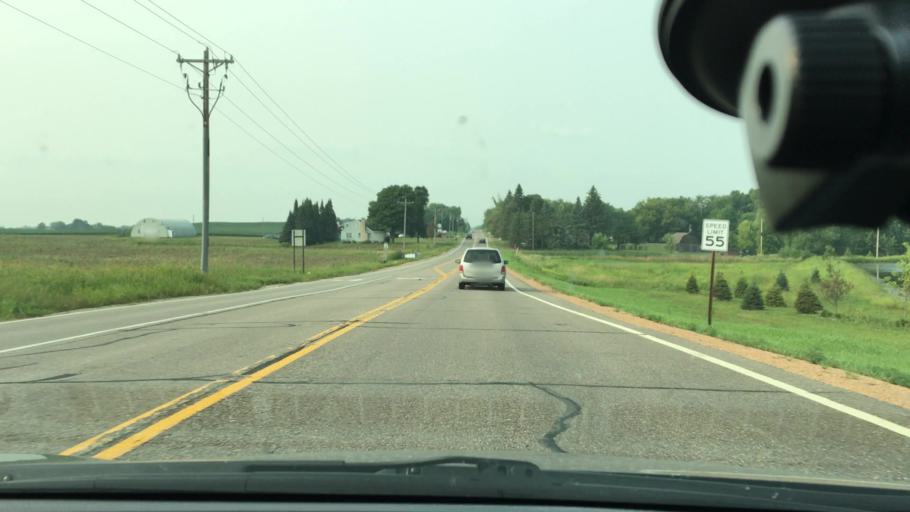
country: US
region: Minnesota
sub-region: Hennepin County
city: Osseo
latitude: 45.1564
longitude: -93.4620
